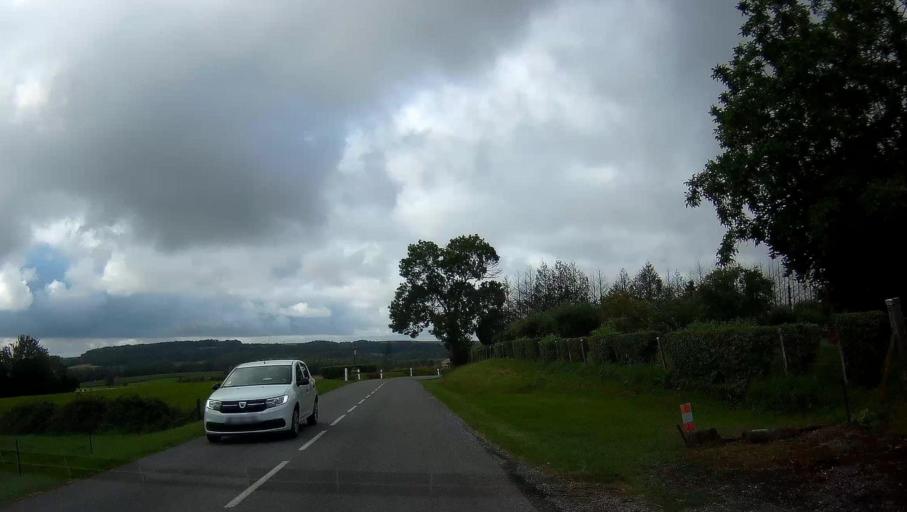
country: FR
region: Champagne-Ardenne
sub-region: Departement des Ardennes
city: Chateau-Porcien
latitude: 49.6452
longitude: 4.2492
